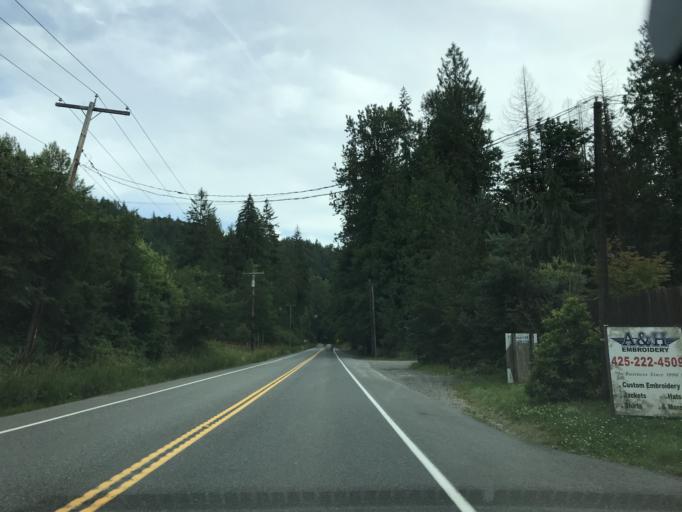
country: US
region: Washington
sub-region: King County
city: Fall City
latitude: 47.5518
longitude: -121.8997
